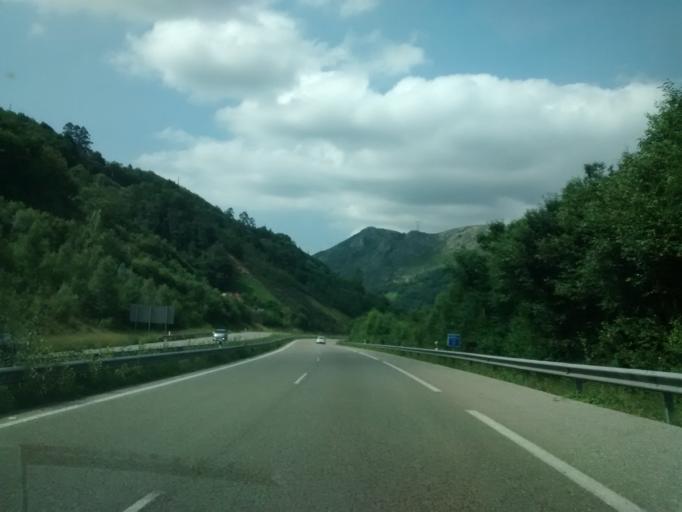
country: ES
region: Asturias
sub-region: Province of Asturias
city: Sama
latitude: 43.3144
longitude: -5.7450
